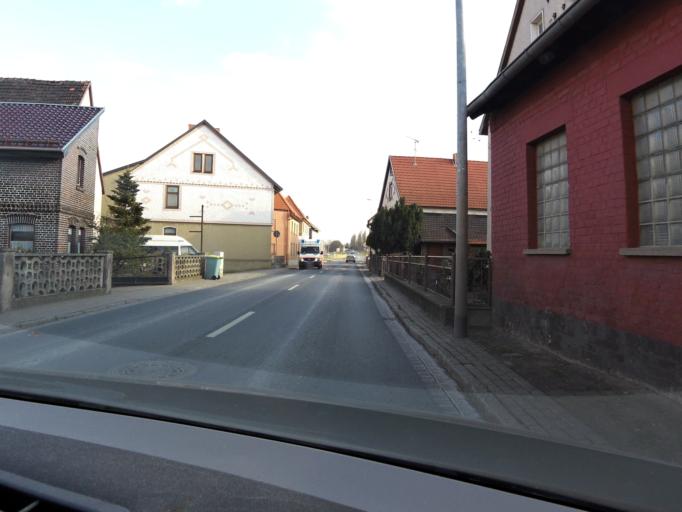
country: DE
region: Thuringia
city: Leimbach
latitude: 50.8212
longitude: 10.1813
